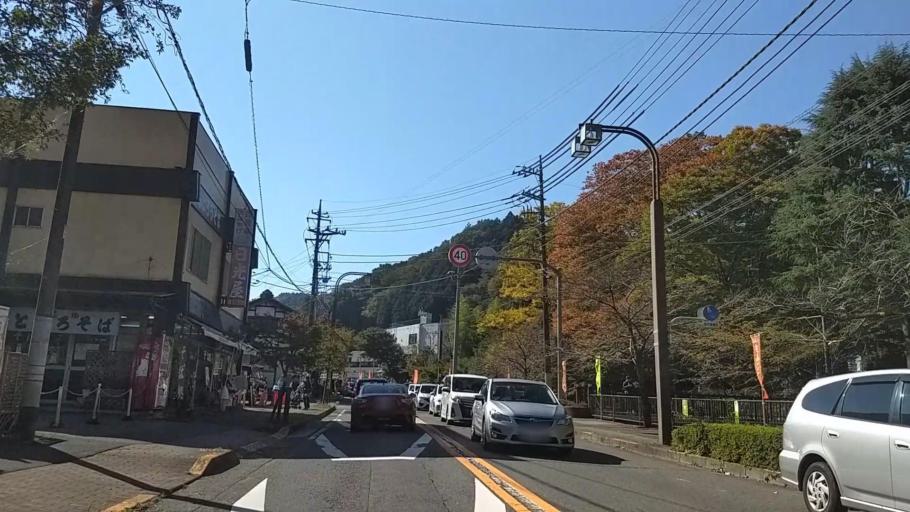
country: JP
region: Tokyo
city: Hachioji
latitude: 35.6319
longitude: 139.2703
